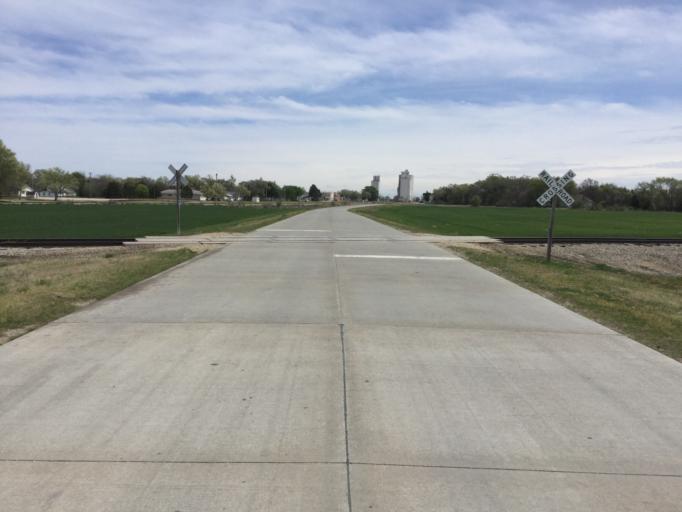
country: US
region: Kansas
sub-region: Osborne County
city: Osborne
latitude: 39.5020
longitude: -98.5526
